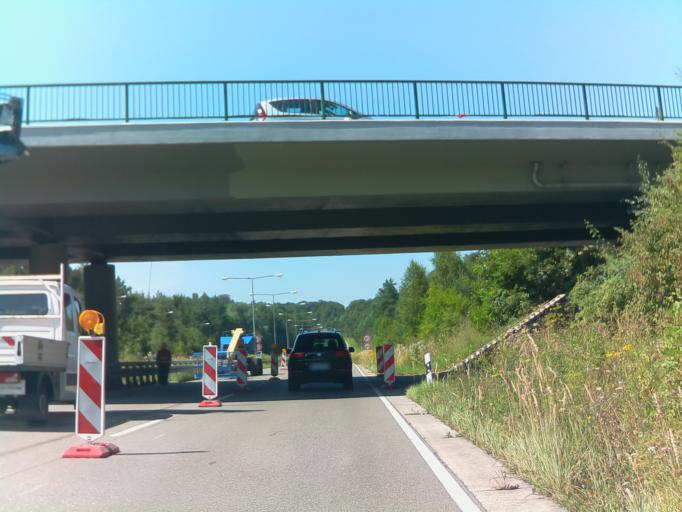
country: DE
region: Baden-Wuerttemberg
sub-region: Regierungsbezirk Stuttgart
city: Gerlingen
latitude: 48.7782
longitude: 9.0906
